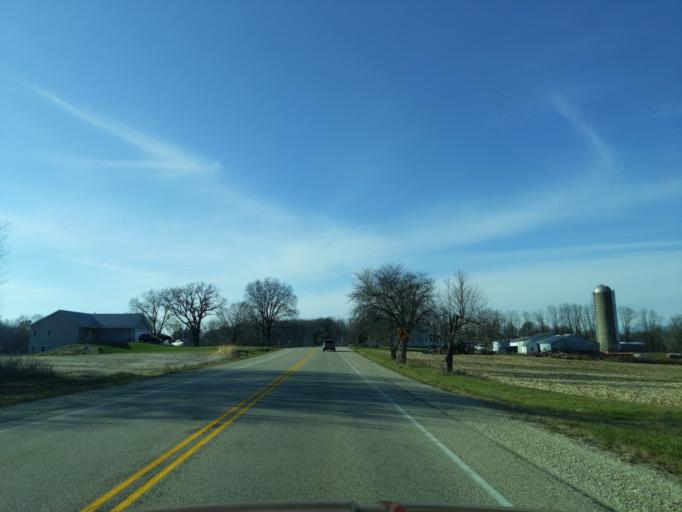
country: US
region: Wisconsin
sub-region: Rock County
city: Milton
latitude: 42.8239
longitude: -88.9418
